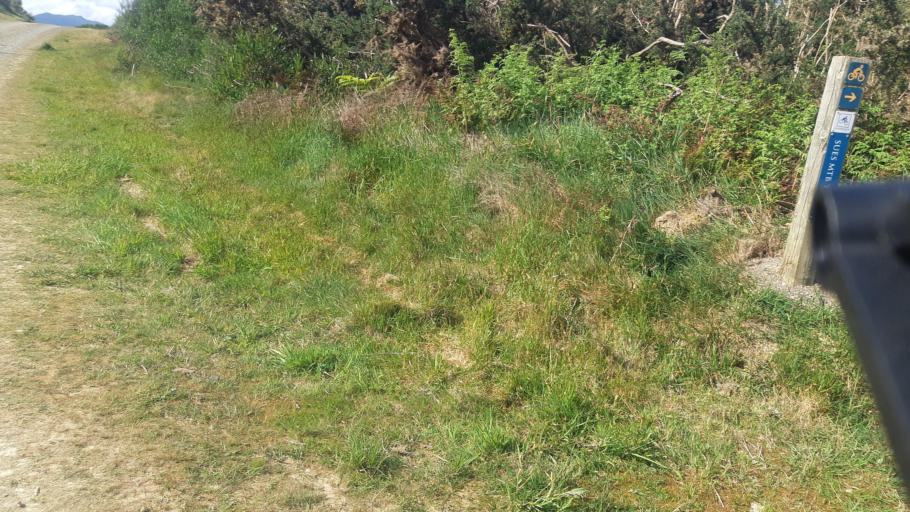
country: NZ
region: Marlborough
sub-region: Marlborough District
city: Picton
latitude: -41.2730
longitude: 174.0204
